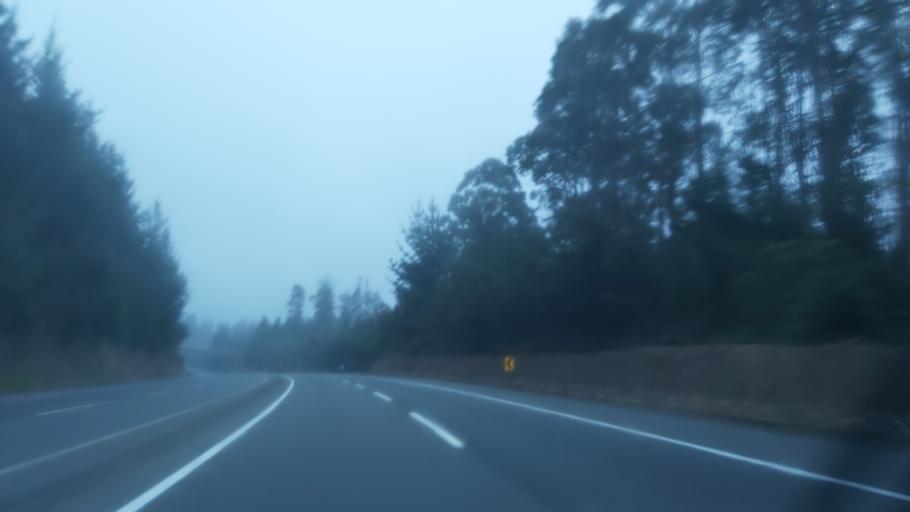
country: CL
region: Biobio
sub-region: Provincia de Concepcion
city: Penco
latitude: -36.7424
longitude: -72.9102
